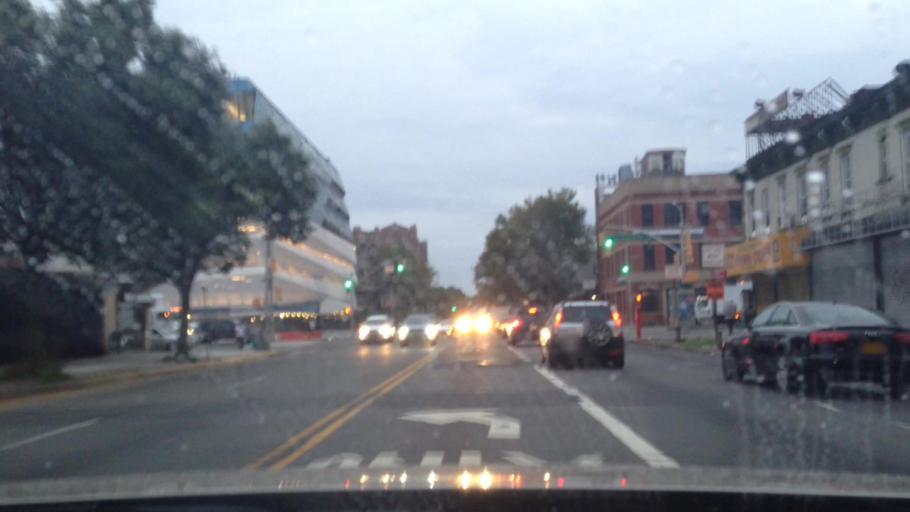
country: US
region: New York
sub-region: Kings County
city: East New York
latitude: 40.6764
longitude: -73.8971
